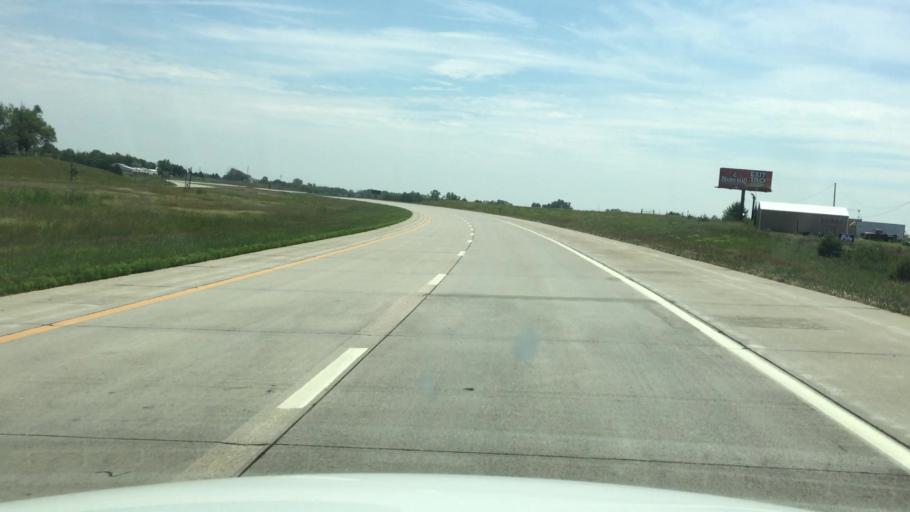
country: US
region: Kansas
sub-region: Jackson County
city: Holton
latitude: 39.3378
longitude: -95.7280
